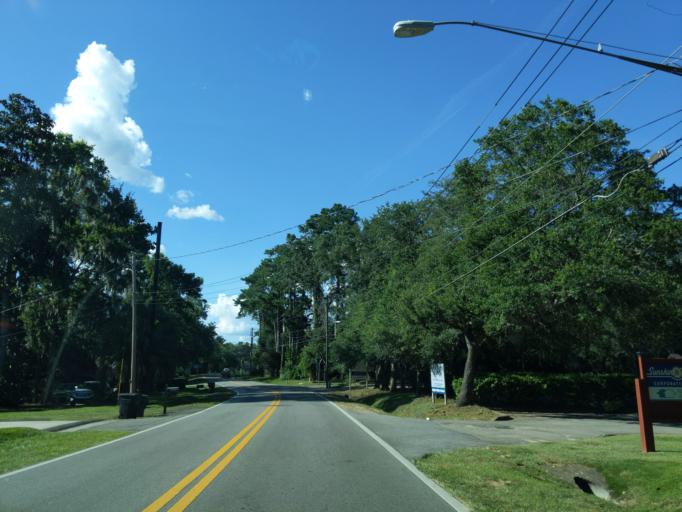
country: US
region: Florida
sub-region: Leon County
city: Tallahassee
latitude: 30.4272
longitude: -84.2435
